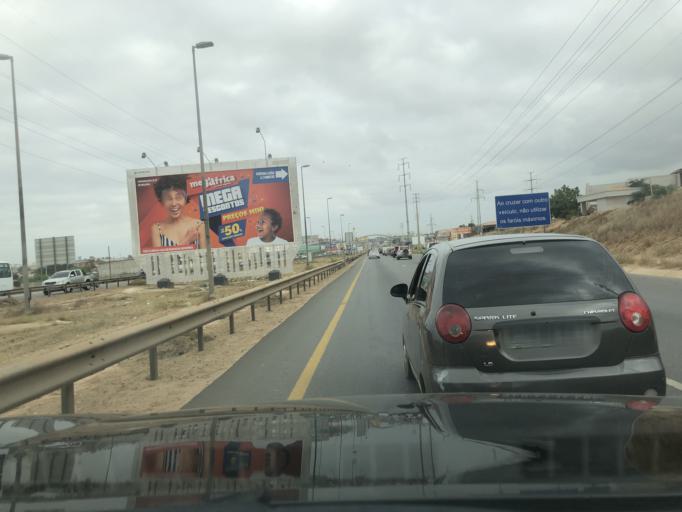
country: AO
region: Luanda
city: Luanda
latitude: -8.9745
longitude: 13.2138
